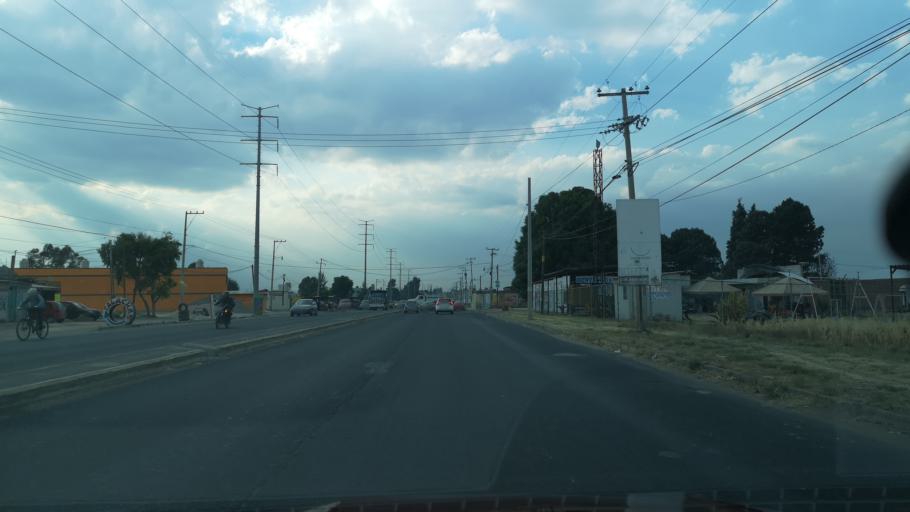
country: MX
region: Puebla
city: Cuanala
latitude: 19.0886
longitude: -98.3344
